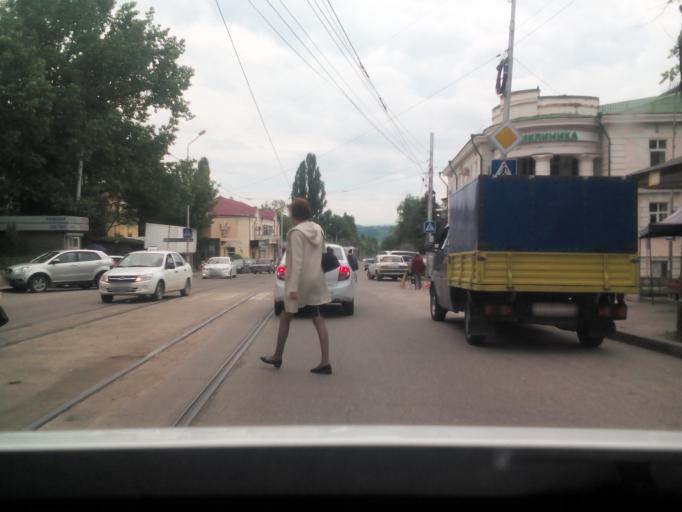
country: RU
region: Stavropol'skiy
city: Pyatigorsk
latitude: 44.0459
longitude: 43.0638
